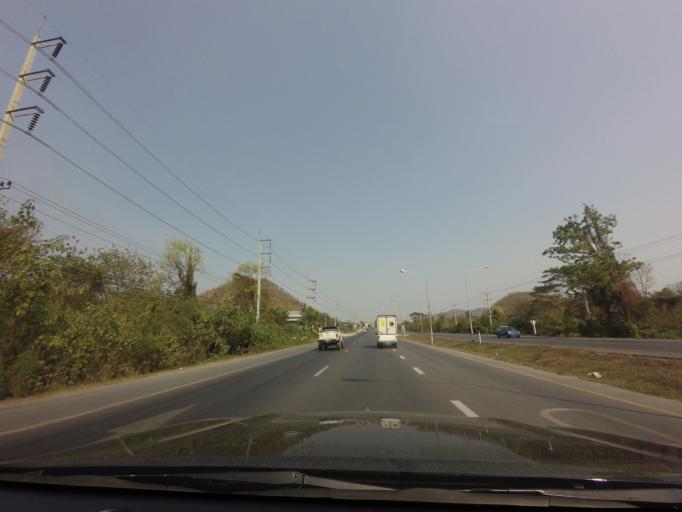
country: TH
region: Kanchanaburi
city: Kanchanaburi
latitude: 14.0400
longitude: 99.5420
